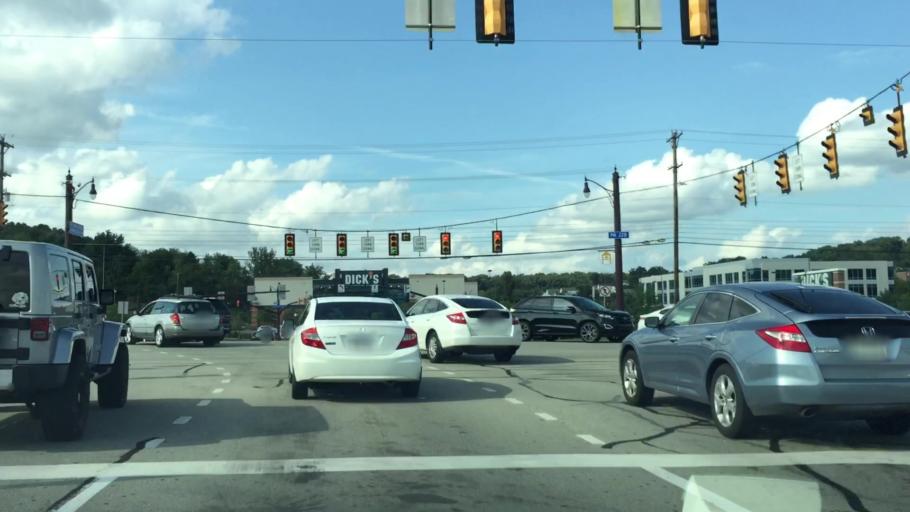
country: US
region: Pennsylvania
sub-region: Butler County
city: Fox Run
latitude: 40.6853
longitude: -80.0876
